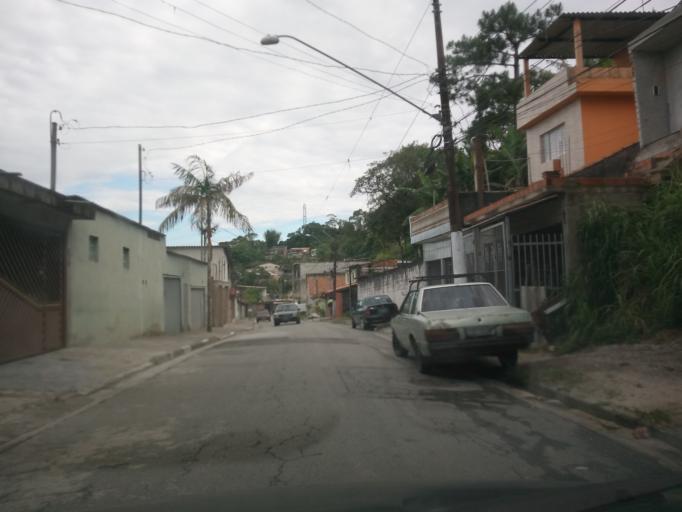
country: BR
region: Sao Paulo
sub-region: Sao Bernardo Do Campo
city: Sao Bernardo do Campo
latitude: -23.8010
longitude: -46.5364
